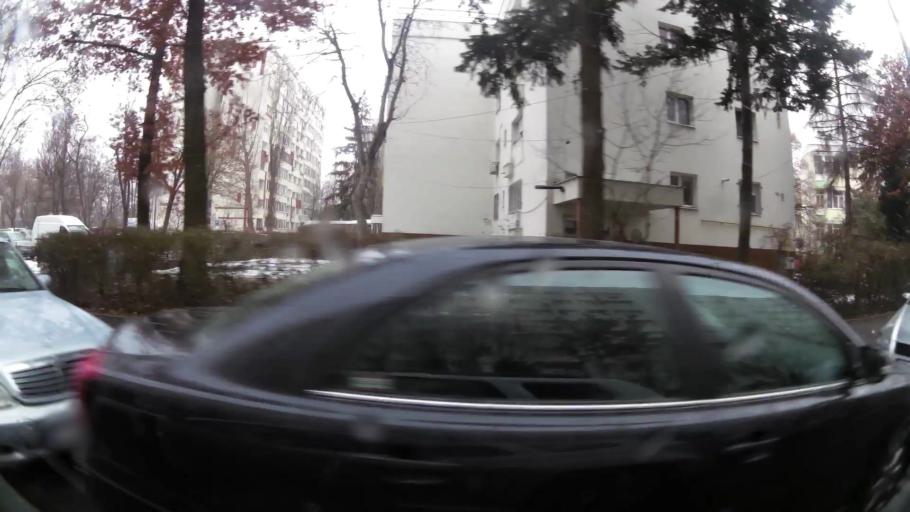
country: RO
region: Ilfov
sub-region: Comuna Chiajna
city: Rosu
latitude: 44.4808
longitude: 26.0531
